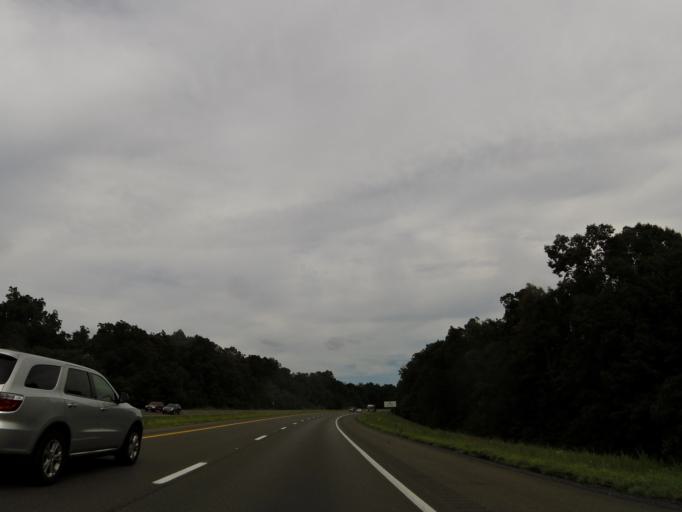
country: US
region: Kentucky
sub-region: Lyon County
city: Eddyville
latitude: 37.0638
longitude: -88.2016
